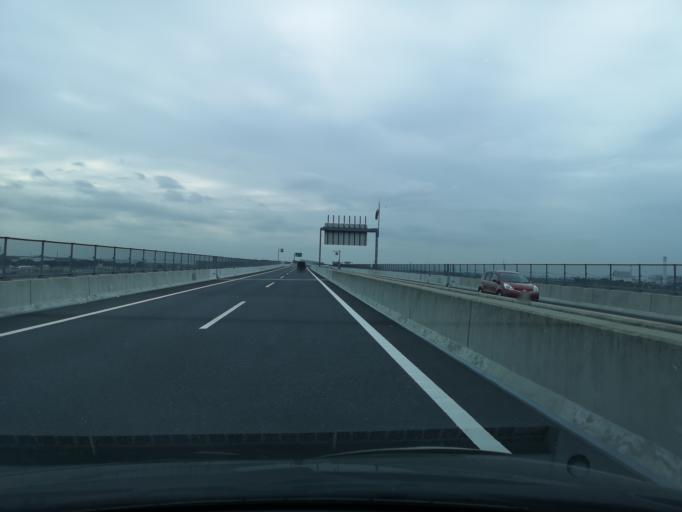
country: JP
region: Kanagawa
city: Atsugi
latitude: 35.3971
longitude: 139.3769
